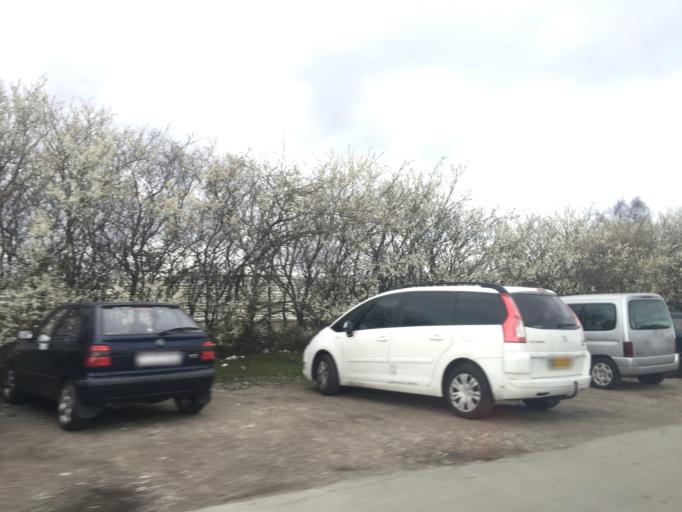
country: DK
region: Capital Region
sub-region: Frederiksberg Kommune
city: Frederiksberg
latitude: 55.6381
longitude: 12.5423
